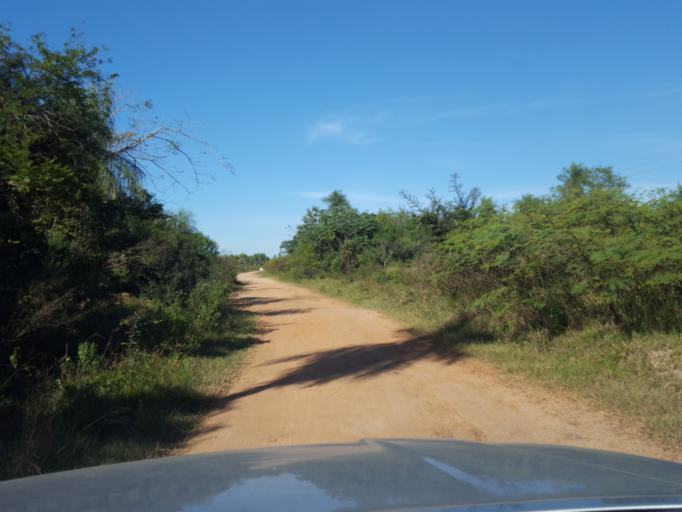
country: PY
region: Cordillera
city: Atyra
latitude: -25.2494
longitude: -57.1198
